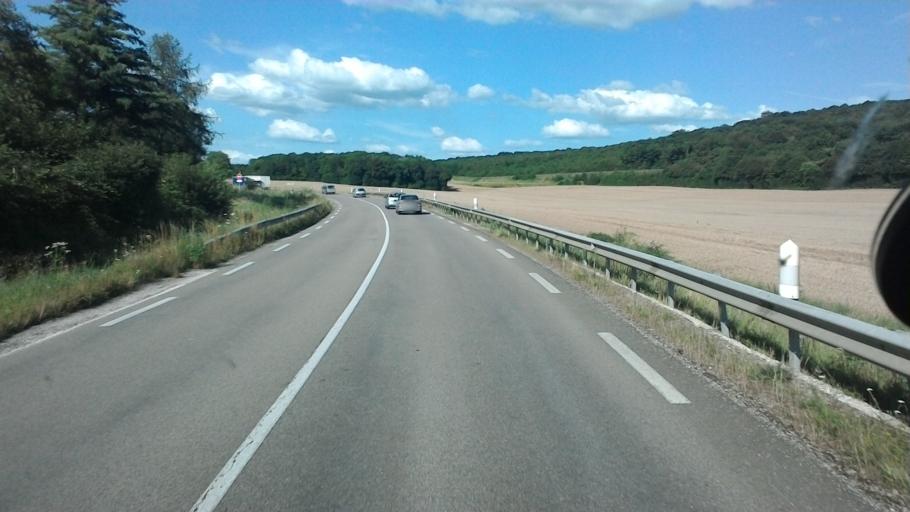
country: FR
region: Franche-Comte
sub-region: Departement de la Haute-Saone
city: Noidans-les-Vesoul
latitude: 47.5912
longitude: 6.1030
